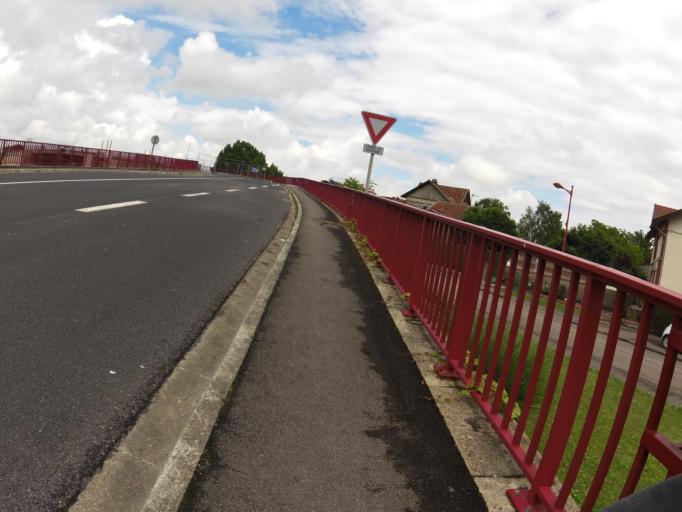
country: FR
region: Lorraine
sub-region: Departement de la Meuse
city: Revigny-sur-Ornain
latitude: 48.8227
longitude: 4.9841
